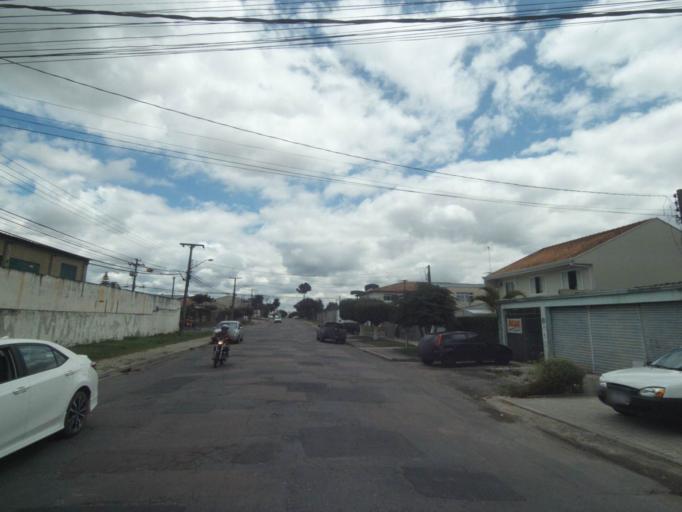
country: BR
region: Parana
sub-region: Curitiba
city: Curitiba
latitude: -25.4942
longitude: -49.2772
